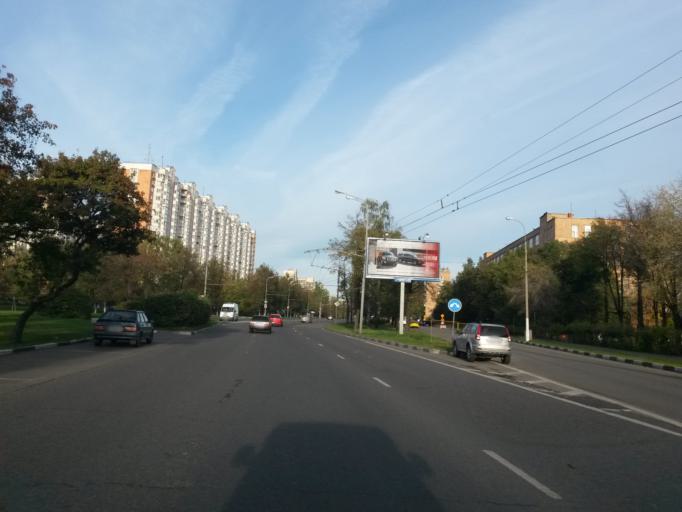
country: RU
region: Moscow
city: Zyuzino
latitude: 55.6716
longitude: 37.5819
